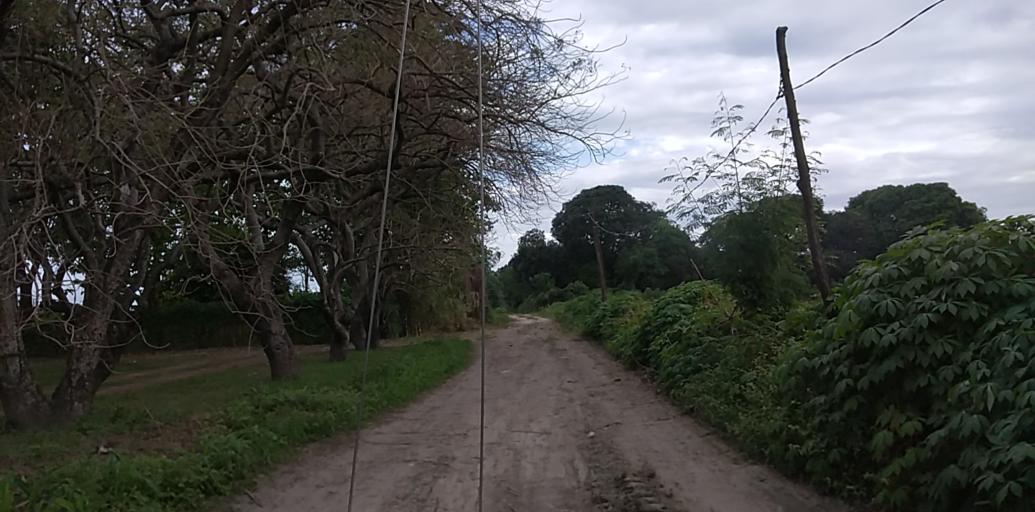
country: PH
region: Central Luzon
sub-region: Province of Pampanga
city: Pulung Santol
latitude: 15.0367
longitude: 120.5606
